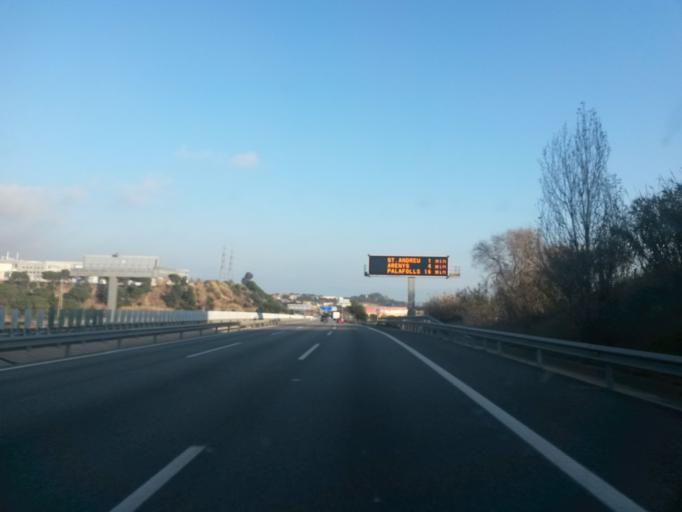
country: ES
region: Catalonia
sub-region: Provincia de Barcelona
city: Mataro
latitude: 41.5553
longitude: 2.4455
